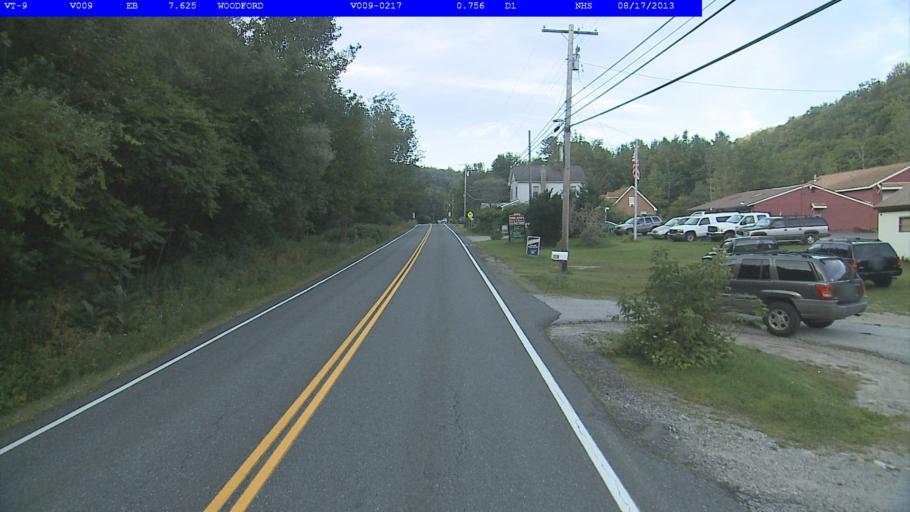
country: US
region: Vermont
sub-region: Bennington County
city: Bennington
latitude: 42.8909
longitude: -73.1395
